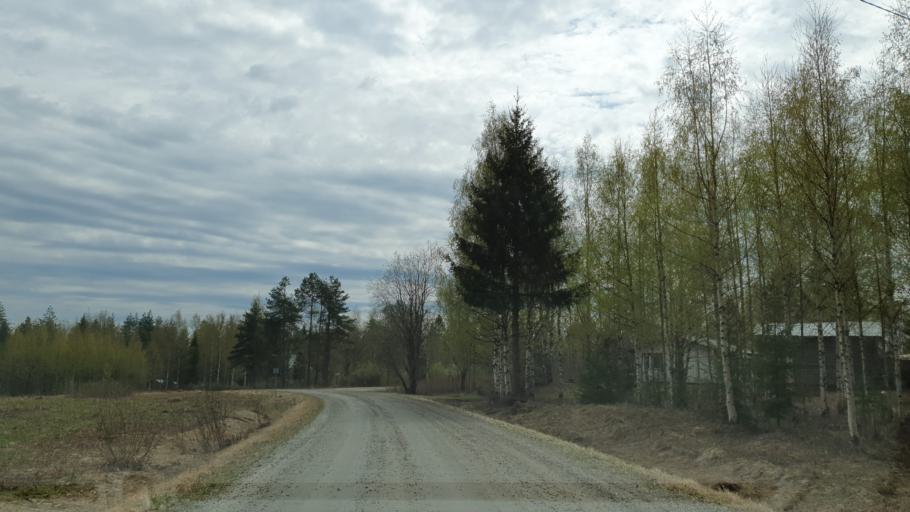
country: FI
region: Kainuu
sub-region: Kehys-Kainuu
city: Kuhmo
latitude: 64.1354
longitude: 29.9705
